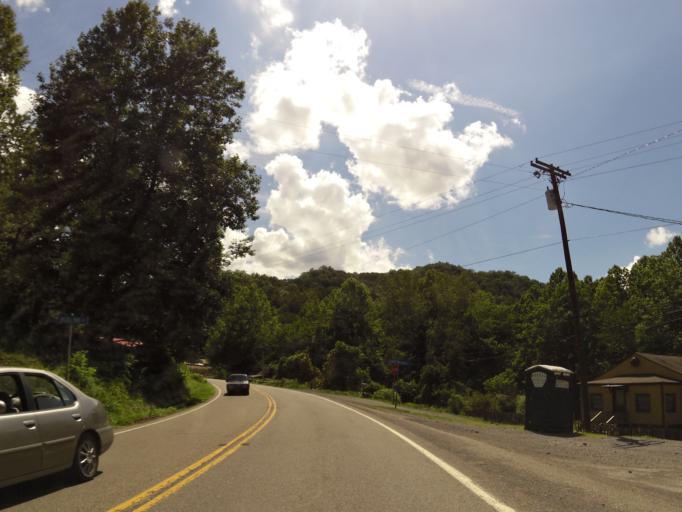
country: US
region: Virginia
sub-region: Lee County
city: Pennington Gap
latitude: 36.7778
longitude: -83.0551
